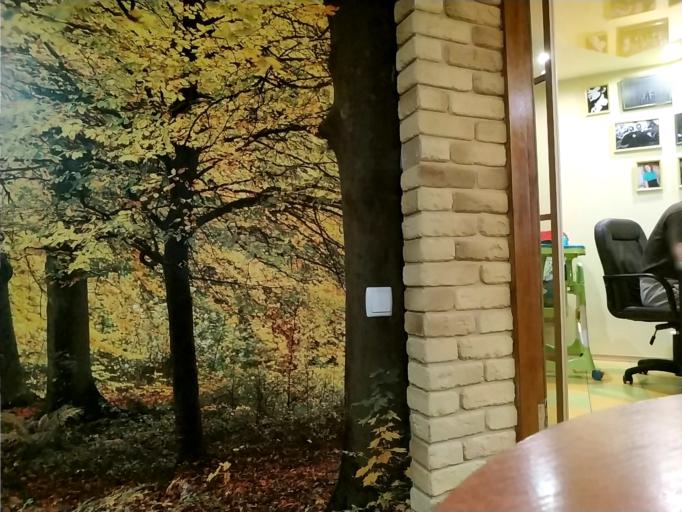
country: RU
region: Tverskaya
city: Zapadnaya Dvina
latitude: 56.3337
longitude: 31.8776
